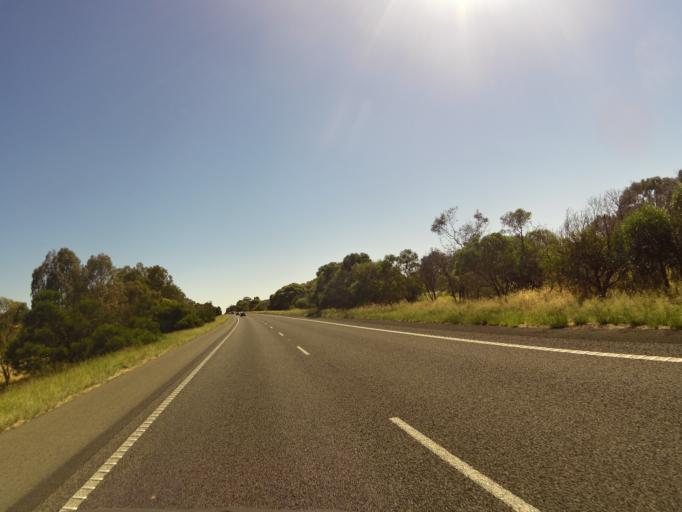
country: AU
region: Victoria
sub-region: Greater Shepparton
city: Shepparton
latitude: -36.8983
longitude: 145.2556
